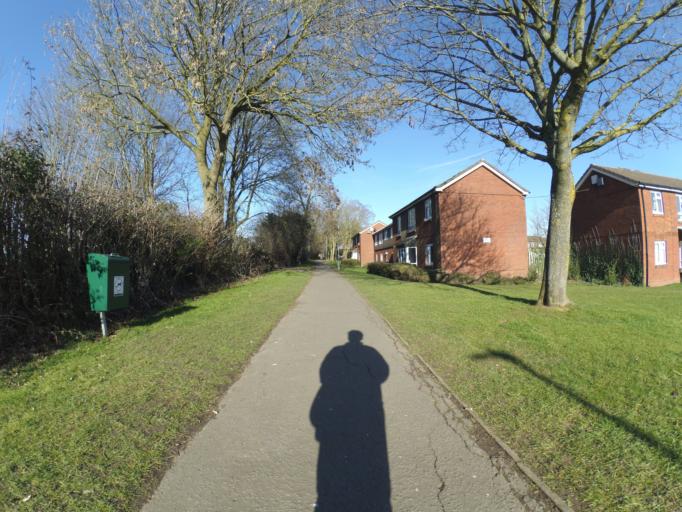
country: GB
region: England
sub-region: Warwickshire
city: Rugby
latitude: 52.3896
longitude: -1.2437
